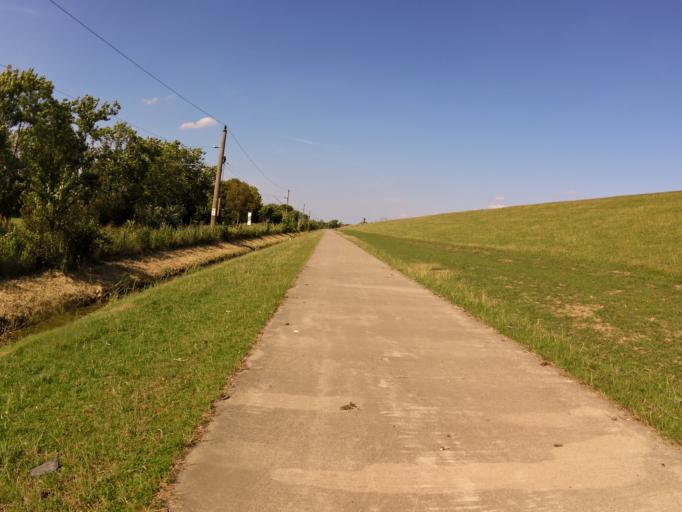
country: DE
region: Lower Saxony
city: Nordenham
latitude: 53.4577
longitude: 8.4749
